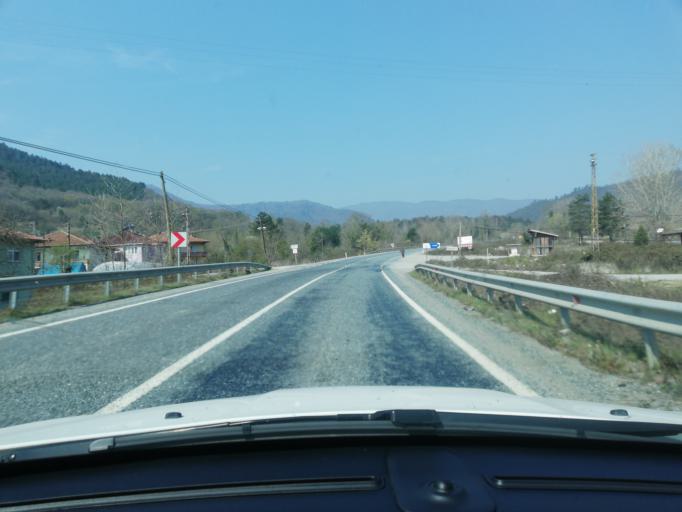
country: TR
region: Zonguldak
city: Gokcebey
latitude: 41.2318
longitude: 32.1979
